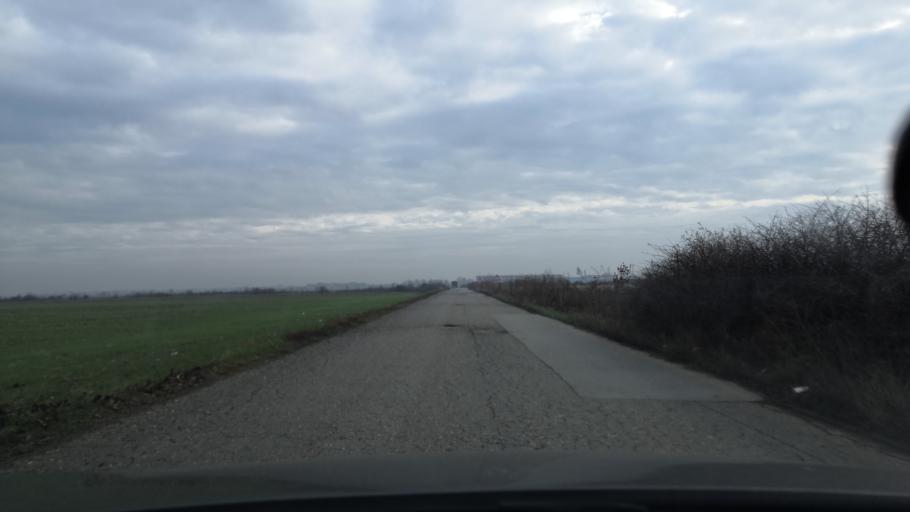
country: RS
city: Ugrinovci
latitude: 44.8815
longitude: 20.1553
